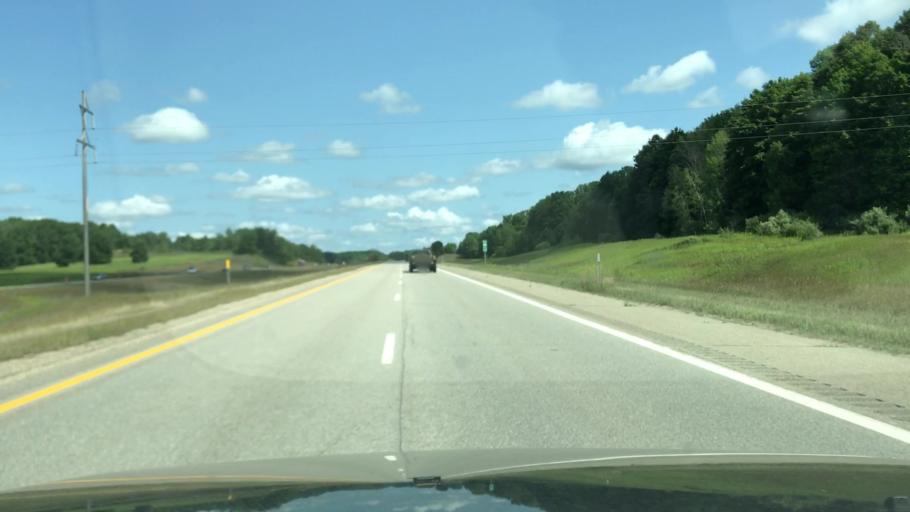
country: US
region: Michigan
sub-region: Osceola County
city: Reed City
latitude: 43.7895
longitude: -85.5339
